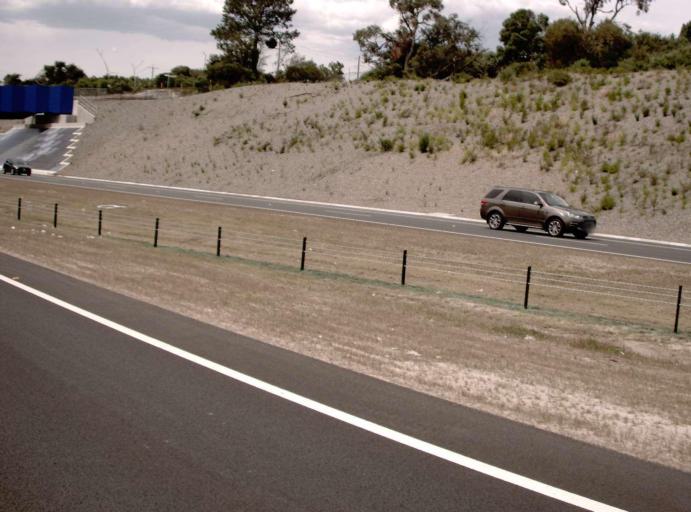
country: AU
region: Victoria
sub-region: Frankston
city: Langwarrin
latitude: -38.1639
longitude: 145.1651
